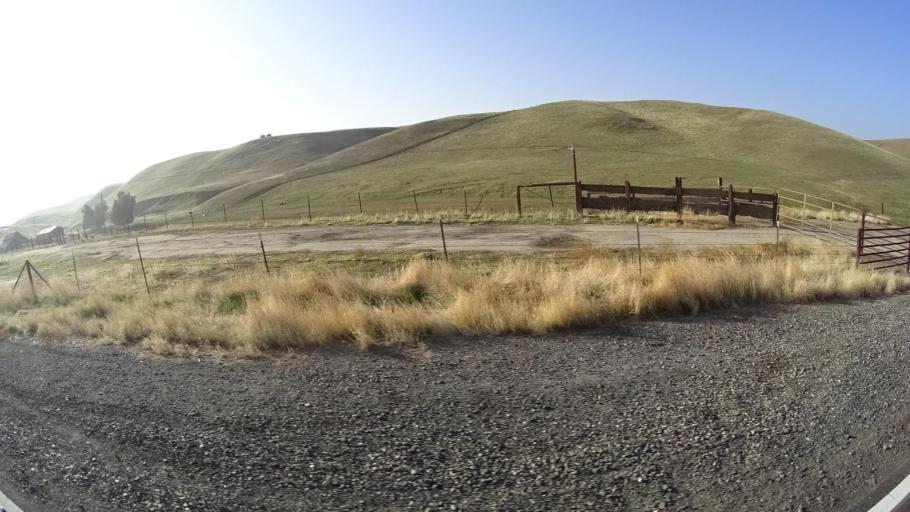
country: US
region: California
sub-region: Tulare County
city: Richgrove
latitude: 35.7461
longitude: -118.9806
